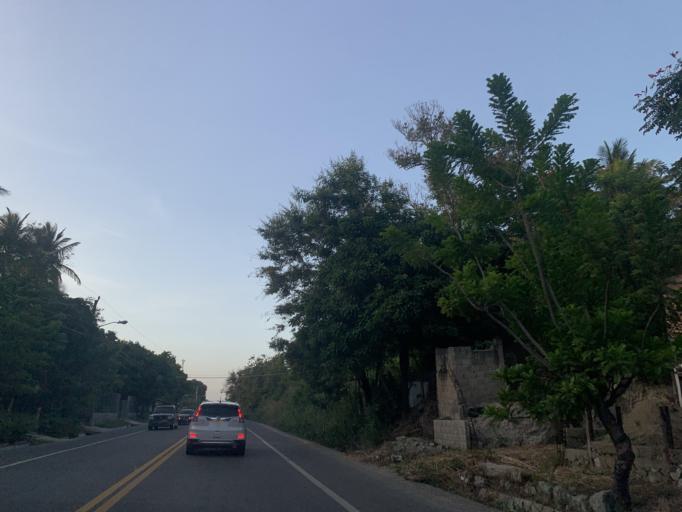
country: DO
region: Puerto Plata
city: Imbert
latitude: 19.7759
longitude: -70.8442
